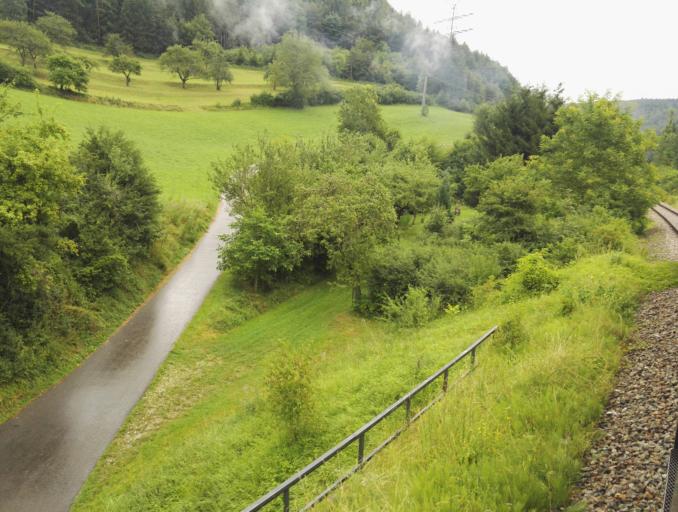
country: DE
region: Baden-Wuerttemberg
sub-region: Freiburg Region
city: Blumberg
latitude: 47.8201
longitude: 8.5559
